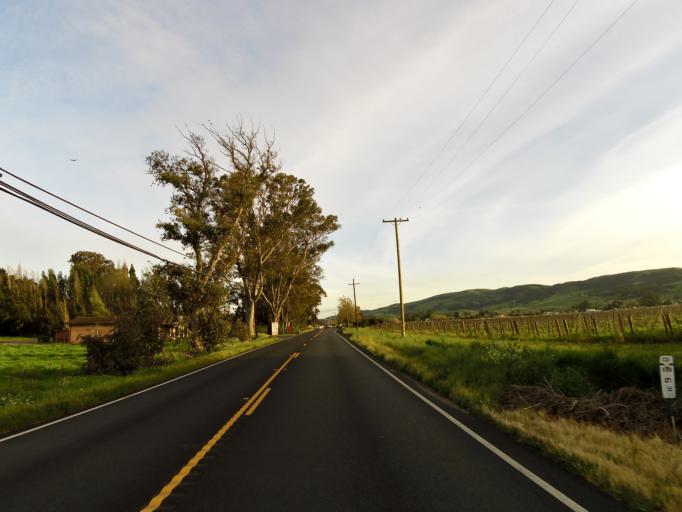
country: US
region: California
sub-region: Sonoma County
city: Temelec
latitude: 38.2306
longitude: -122.4595
